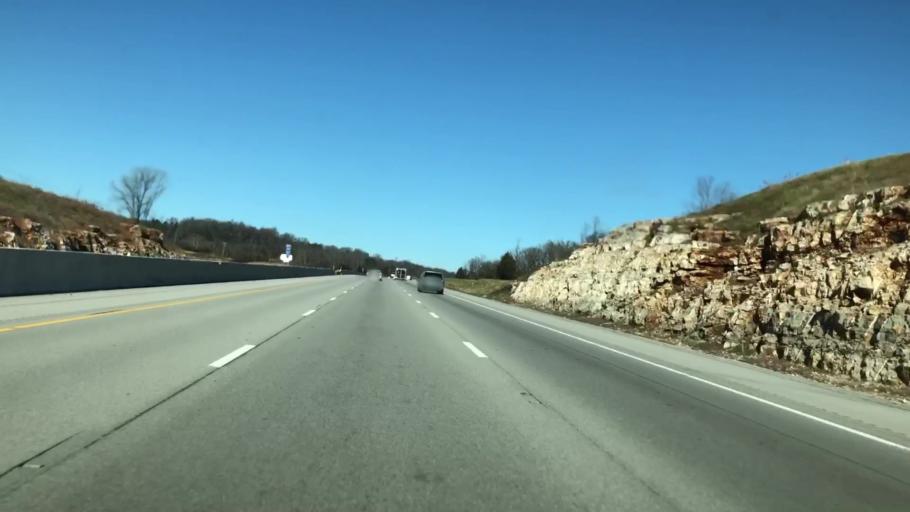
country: US
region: Kentucky
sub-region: Hart County
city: Munfordville
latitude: 37.2556
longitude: -85.9240
